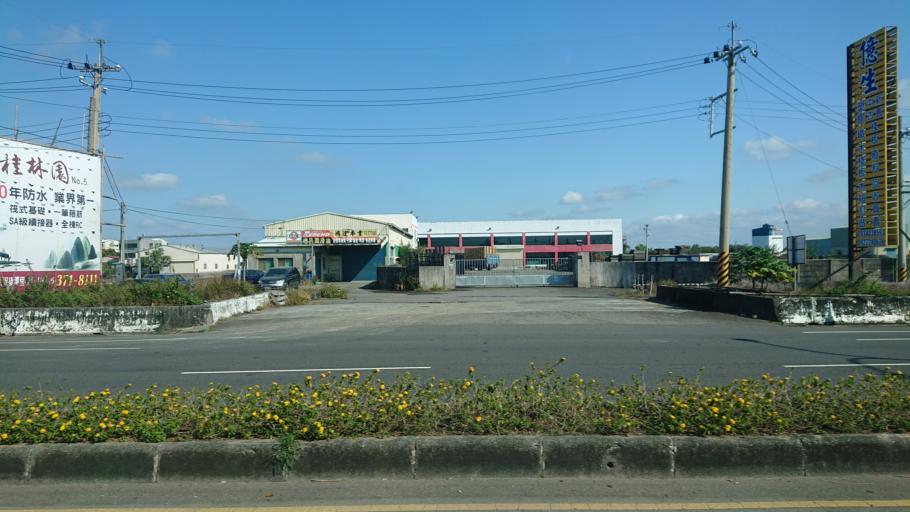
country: TW
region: Taiwan
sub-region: Chiayi
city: Taibao
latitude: 23.4462
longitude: 120.3625
